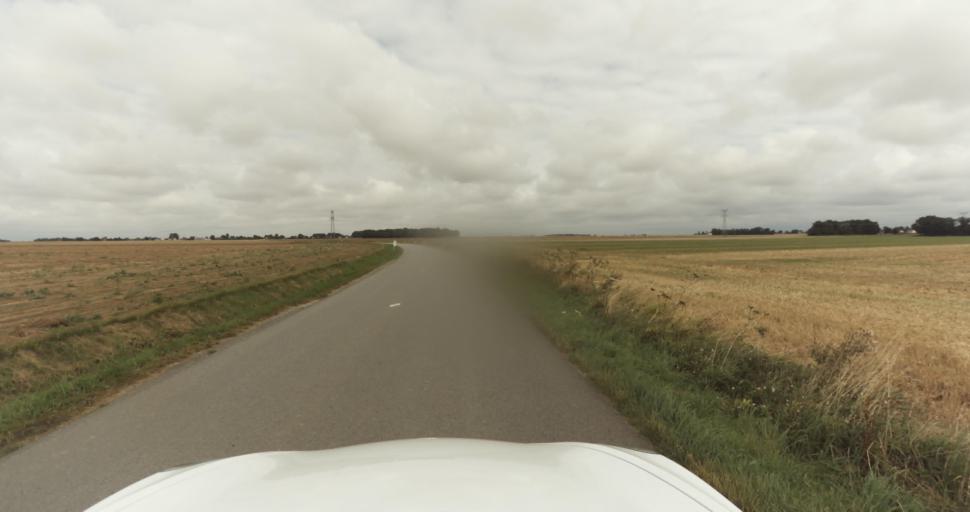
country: FR
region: Haute-Normandie
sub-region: Departement de l'Eure
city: Claville
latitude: 49.0322
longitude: 1.0302
